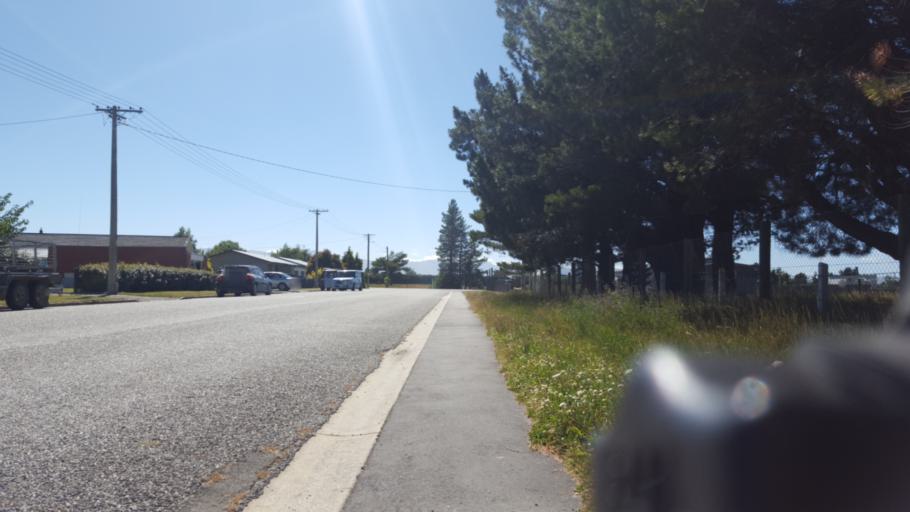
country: NZ
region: Otago
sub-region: Dunedin City
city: Dunedin
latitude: -45.1237
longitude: 170.0991
